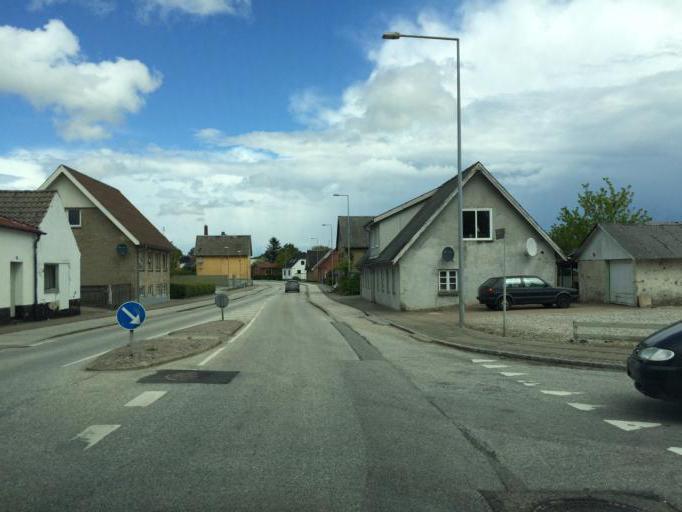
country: DK
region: North Denmark
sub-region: Vesthimmerland Kommune
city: Farso
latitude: 56.7651
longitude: 9.3388
